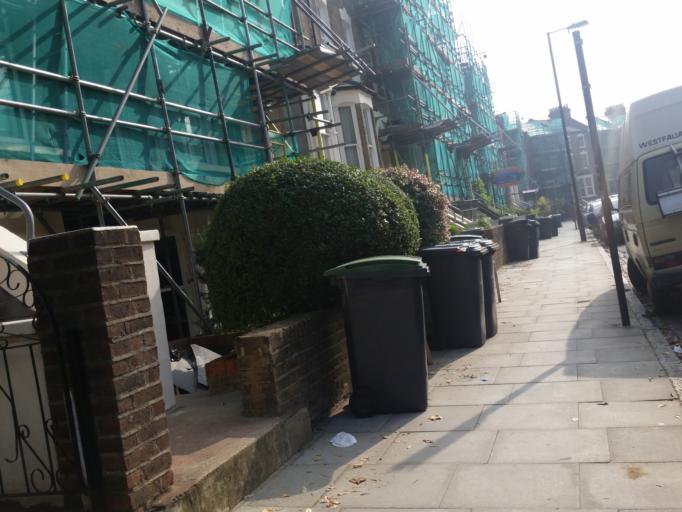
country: GB
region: England
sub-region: Greater London
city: Harringay
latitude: 51.5682
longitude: -0.1069
